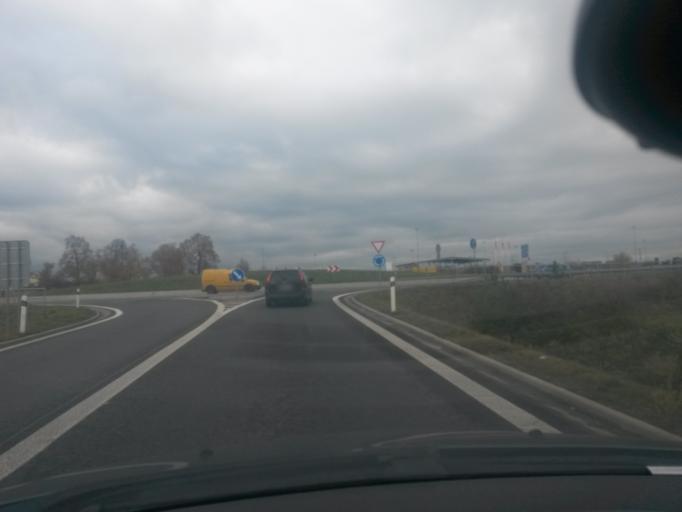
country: CZ
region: Central Bohemia
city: Jesenice
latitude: 49.9629
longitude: 14.5204
